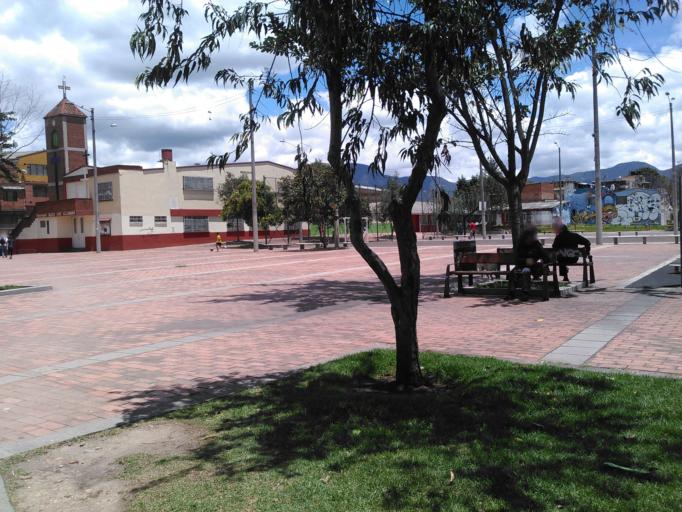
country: CO
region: Bogota D.C.
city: Bogota
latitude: 4.6182
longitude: -74.1240
